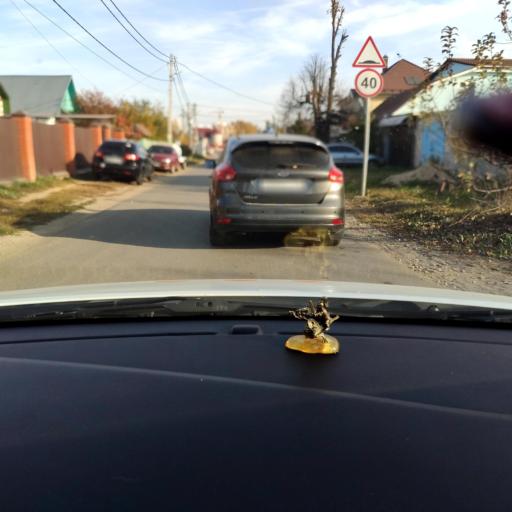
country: RU
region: Tatarstan
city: Osinovo
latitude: 55.8482
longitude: 48.8896
